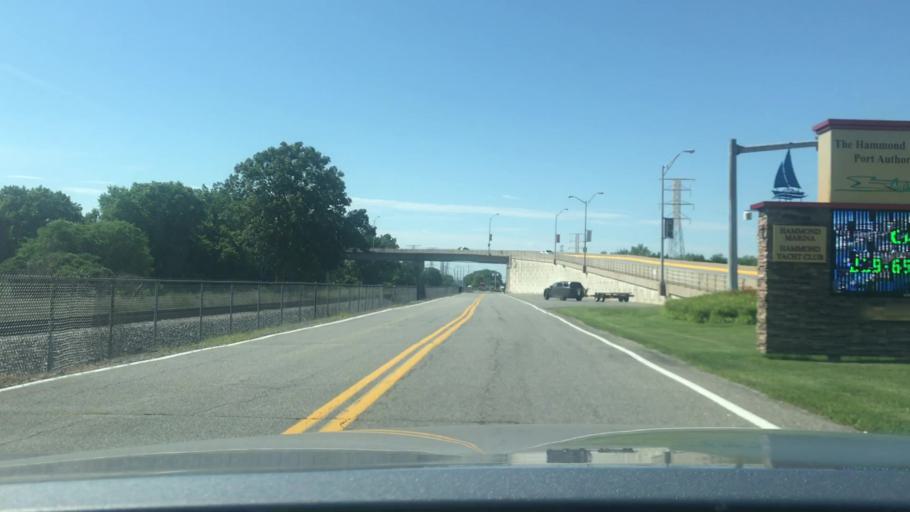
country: US
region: Indiana
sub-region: Lake County
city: Whiting
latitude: 41.6947
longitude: -87.5106
